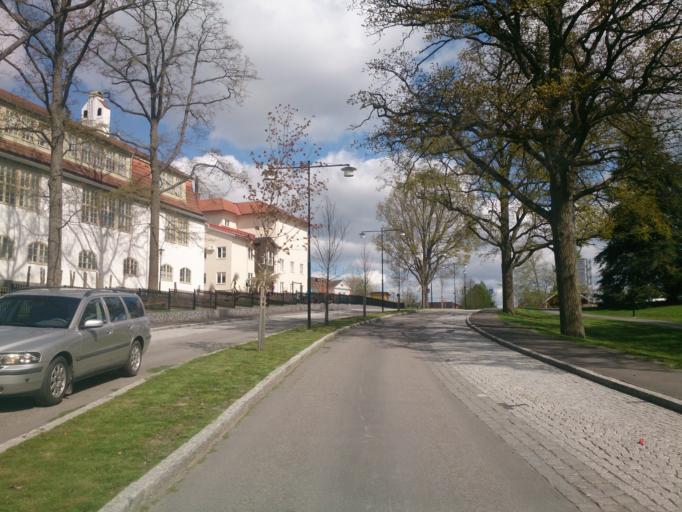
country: SE
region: OEstergoetland
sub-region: Atvidabergs Kommun
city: Atvidaberg
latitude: 58.1975
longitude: 15.9943
